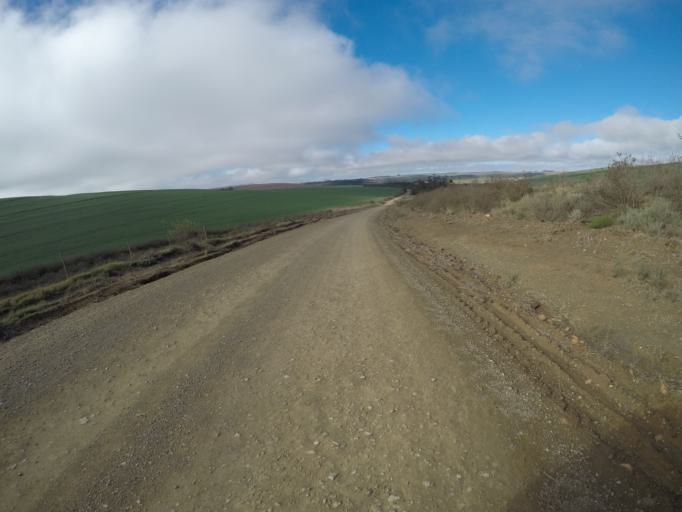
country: ZA
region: Western Cape
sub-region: Overberg District Municipality
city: Caledon
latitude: -34.1096
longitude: 19.7672
